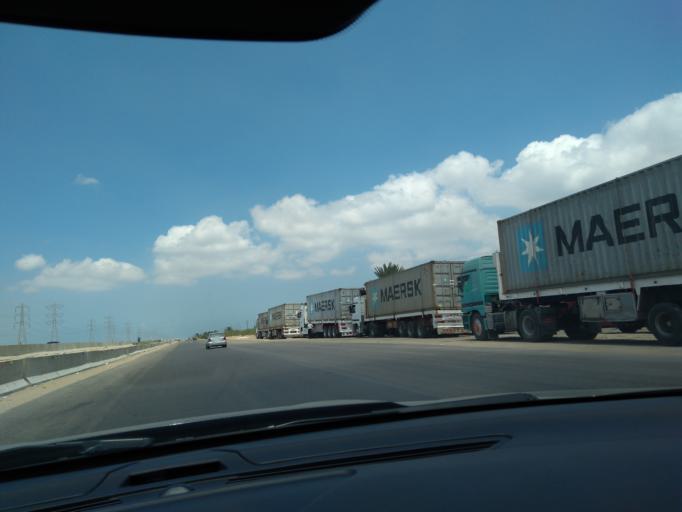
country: EG
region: Muhafazat Bur Sa`id
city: Port Said
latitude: 31.1573
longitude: 32.3021
